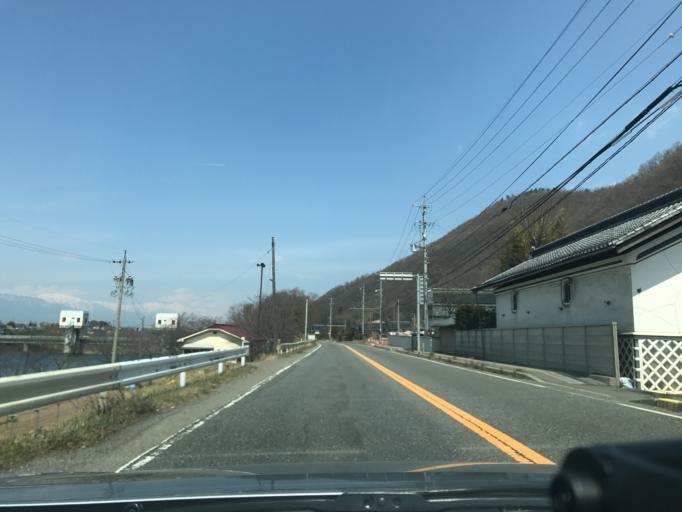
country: JP
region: Nagano
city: Matsumoto
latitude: 36.2522
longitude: 137.9513
